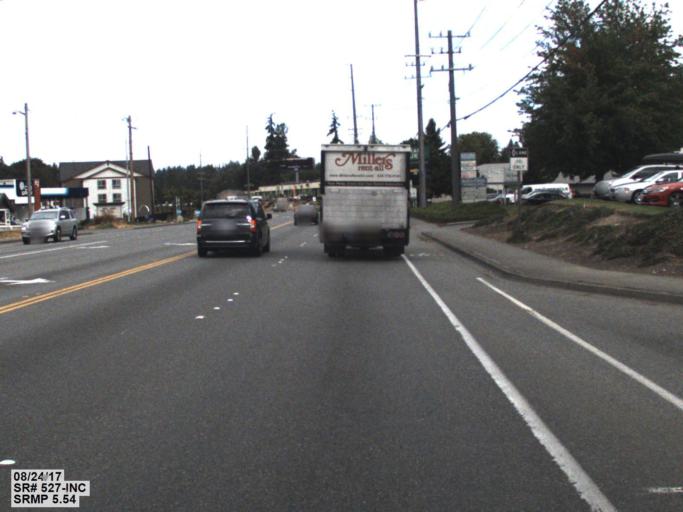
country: US
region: Washington
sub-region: Snohomish County
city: Mill Creek
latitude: 47.8350
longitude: -122.2109
